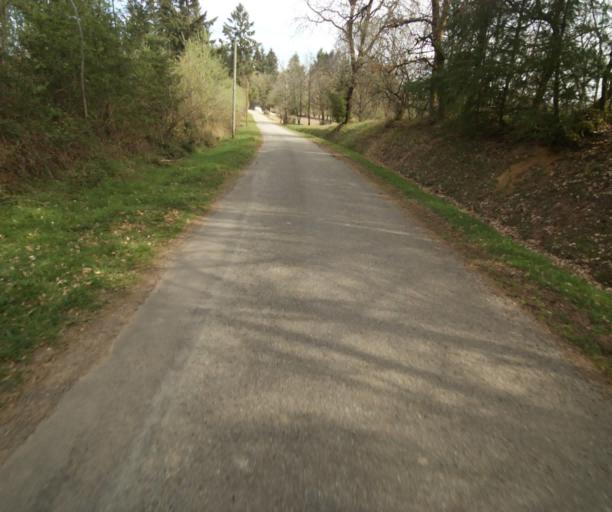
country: FR
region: Limousin
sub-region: Departement de la Correze
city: Correze
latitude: 45.3806
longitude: 1.8219
